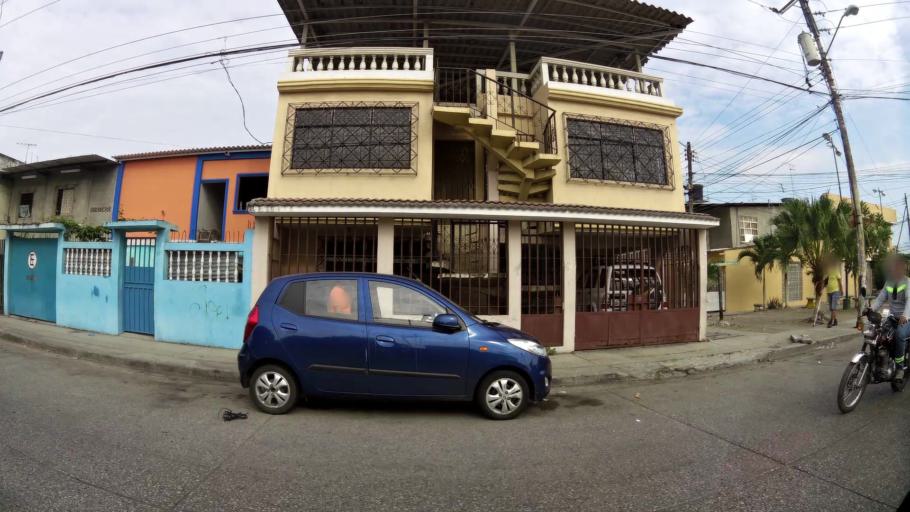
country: EC
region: Guayas
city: Guayaquil
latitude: -2.2489
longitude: -79.8847
